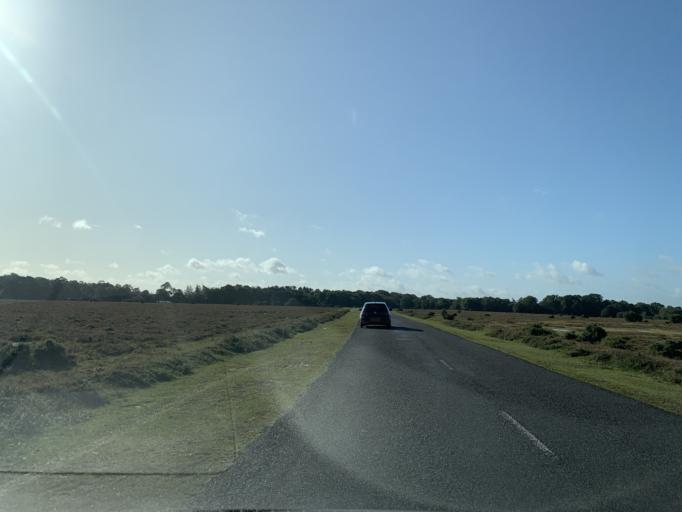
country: GB
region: England
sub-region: Wiltshire
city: Whiteparish
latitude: 50.9366
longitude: -1.6544
